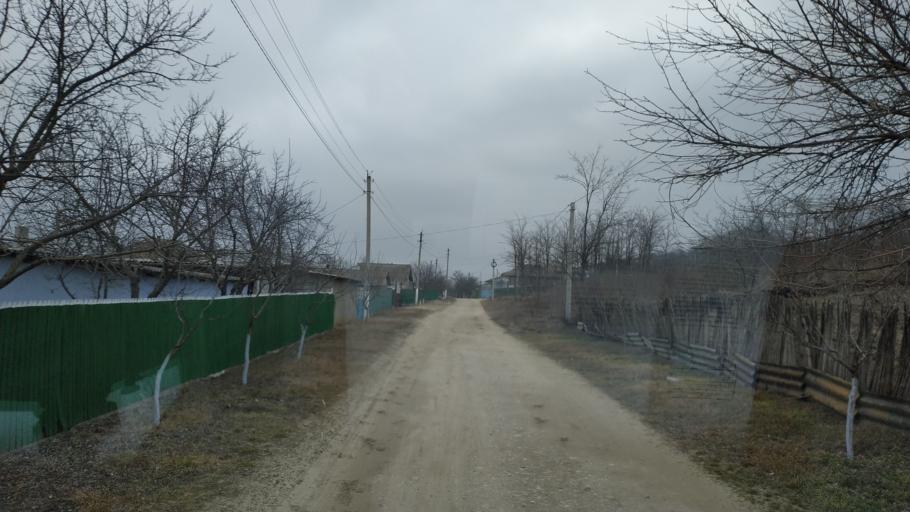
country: MD
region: Hincesti
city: Hincesti
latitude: 46.8882
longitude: 28.4050
